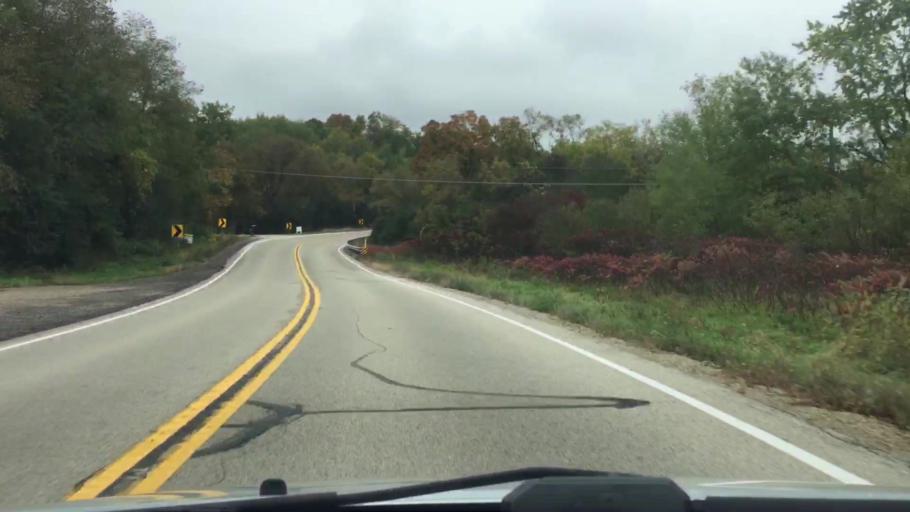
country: US
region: Wisconsin
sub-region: Waukesha County
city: Eagle
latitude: 42.9013
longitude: -88.4736
